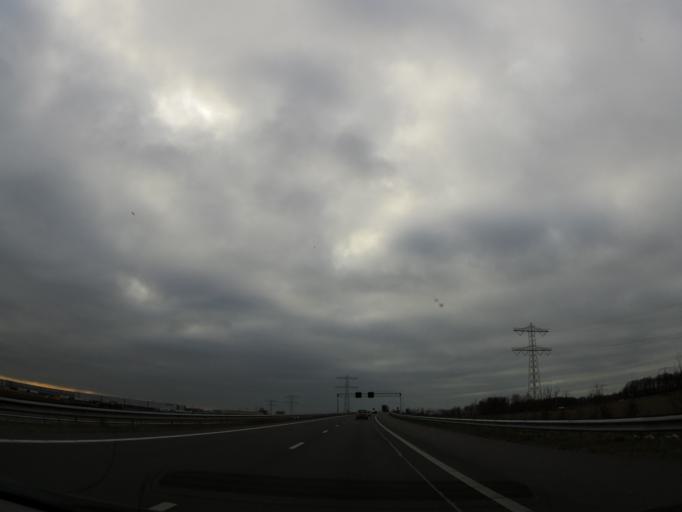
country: NL
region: Limburg
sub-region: Gemeente Maasgouw
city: Maasbracht
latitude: 51.1275
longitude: 5.8951
